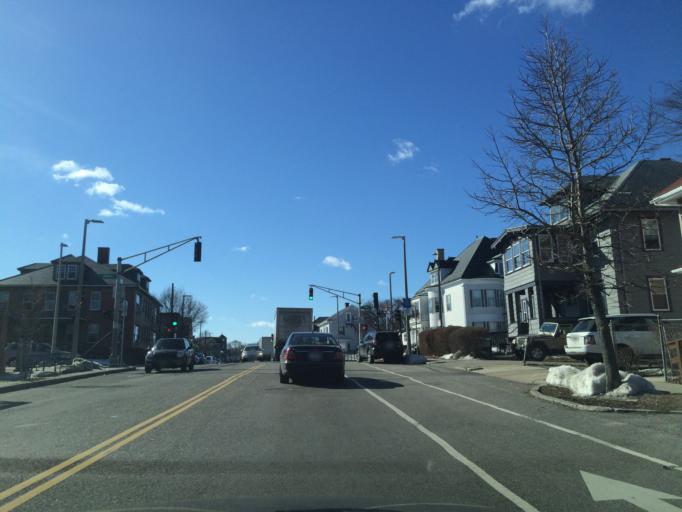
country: US
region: Massachusetts
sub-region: Norfolk County
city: Brookline
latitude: 42.3221
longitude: -71.1122
